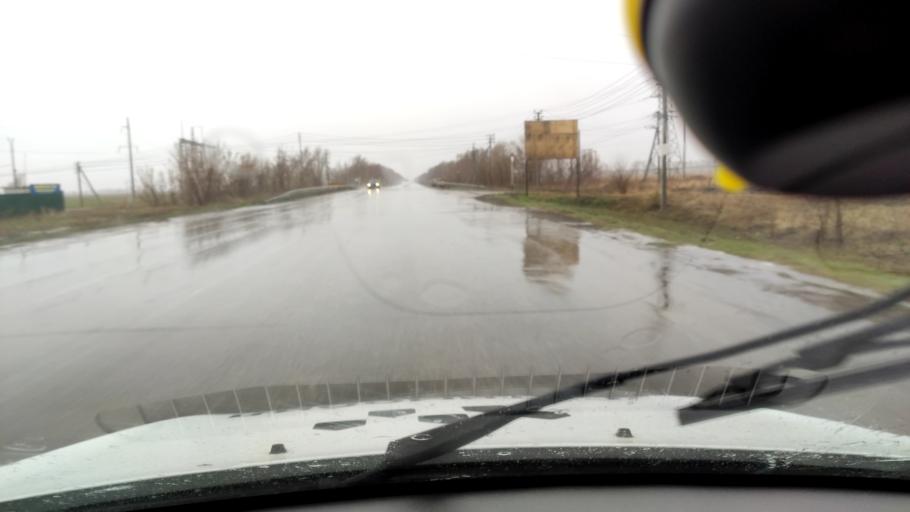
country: RU
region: Samara
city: Tol'yatti
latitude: 53.5854
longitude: 49.4048
